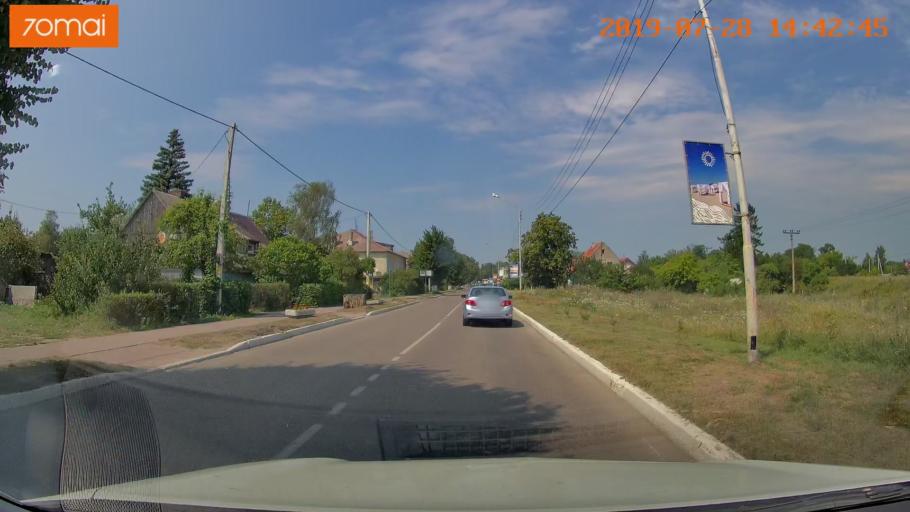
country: RU
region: Kaliningrad
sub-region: Gorod Kaliningrad
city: Yantarnyy
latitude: 54.8617
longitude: 19.9409
